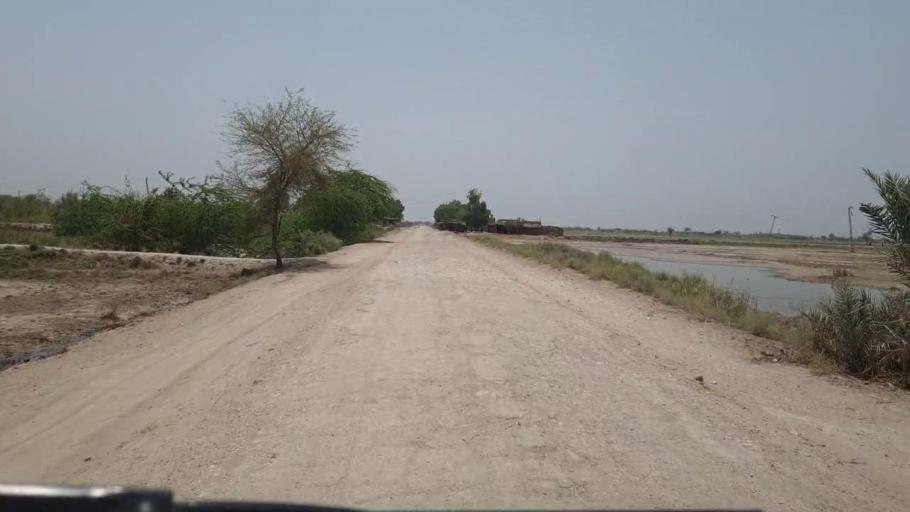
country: PK
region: Sindh
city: Daur
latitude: 26.4600
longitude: 68.1509
